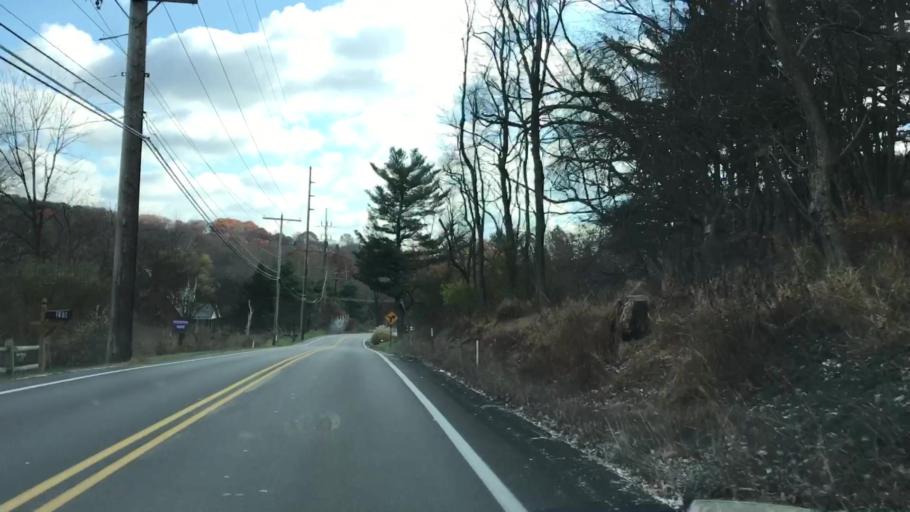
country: US
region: Pennsylvania
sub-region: Allegheny County
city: Franklin Park
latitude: 40.5926
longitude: -80.0566
